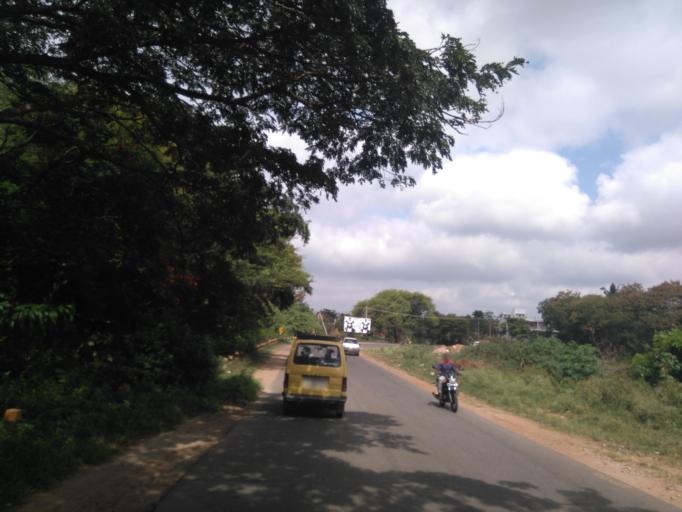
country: IN
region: Karnataka
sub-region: Mysore
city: Mysore
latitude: 12.2923
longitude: 76.7073
